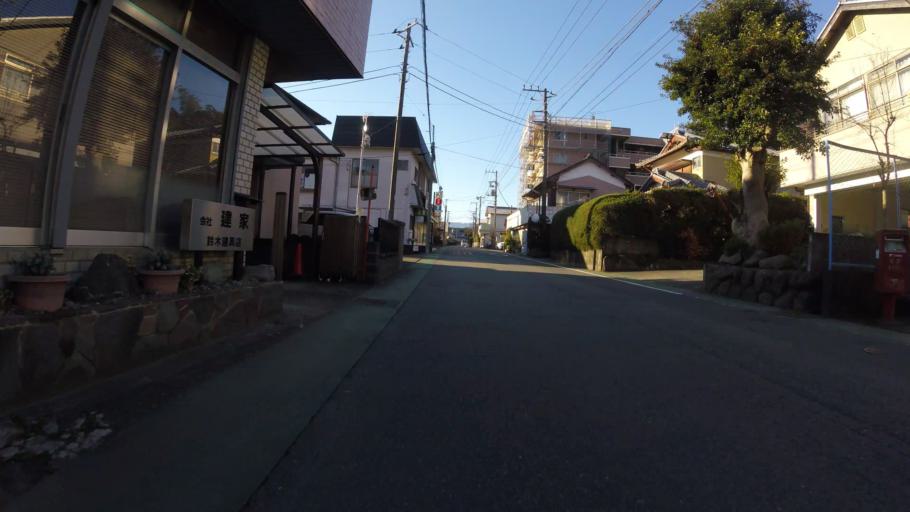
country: JP
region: Shizuoka
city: Ito
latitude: 34.9685
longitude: 138.9432
